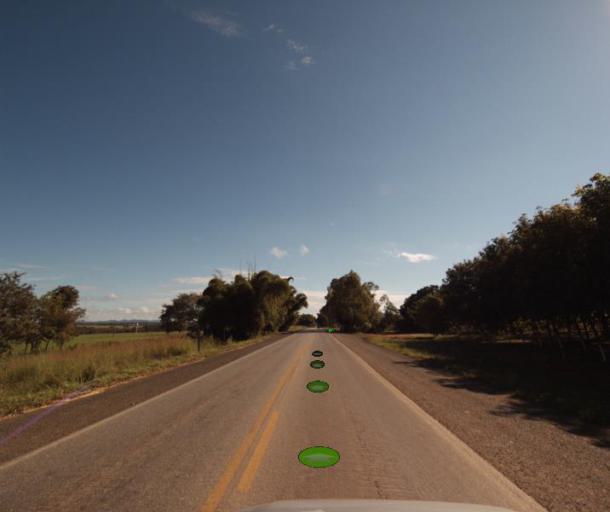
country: BR
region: Goias
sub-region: Uruacu
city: Uruacu
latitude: -14.6308
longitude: -49.1743
